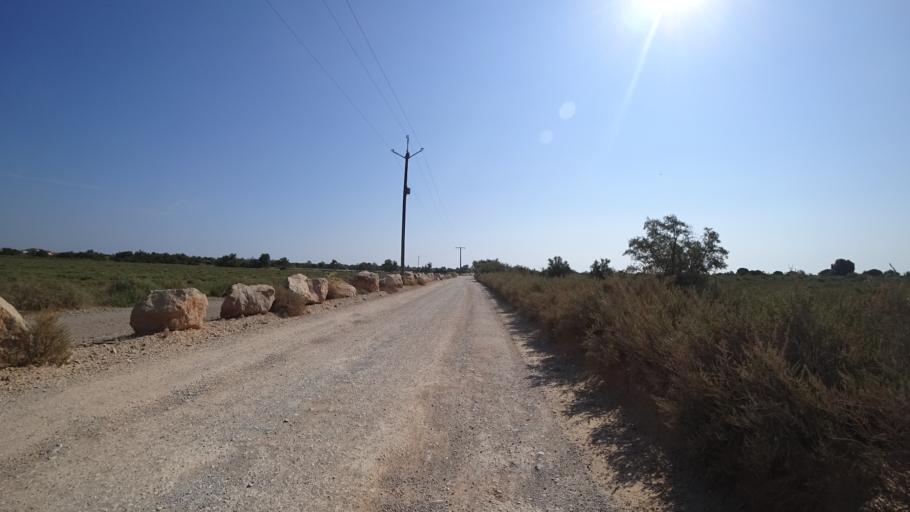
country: FR
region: Languedoc-Roussillon
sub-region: Departement des Pyrenees-Orientales
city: Torreilles
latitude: 42.7566
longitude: 3.0222
